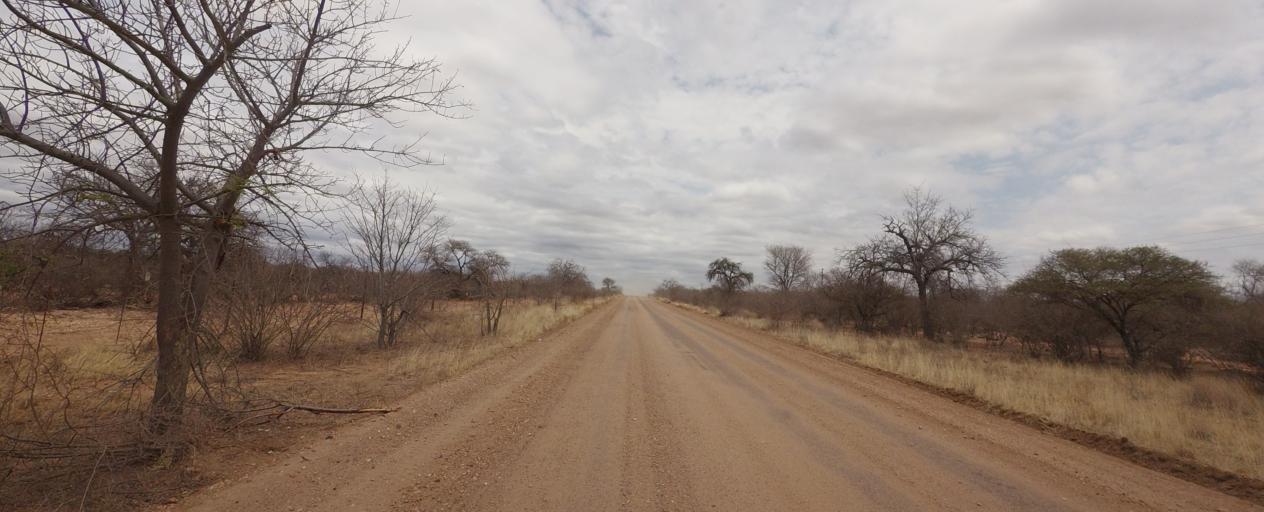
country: BW
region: Central
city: Mathathane
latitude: -22.6771
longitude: 28.6683
